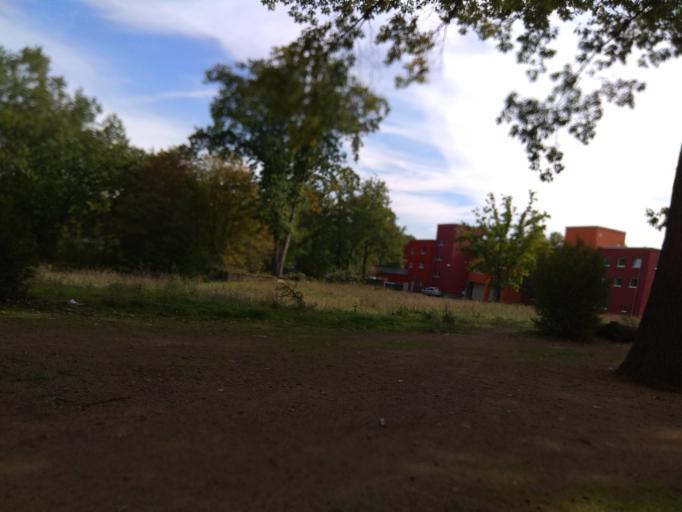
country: DE
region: North Rhine-Westphalia
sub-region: Regierungsbezirk Munster
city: Klein Reken
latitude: 51.7306
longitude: 7.0440
